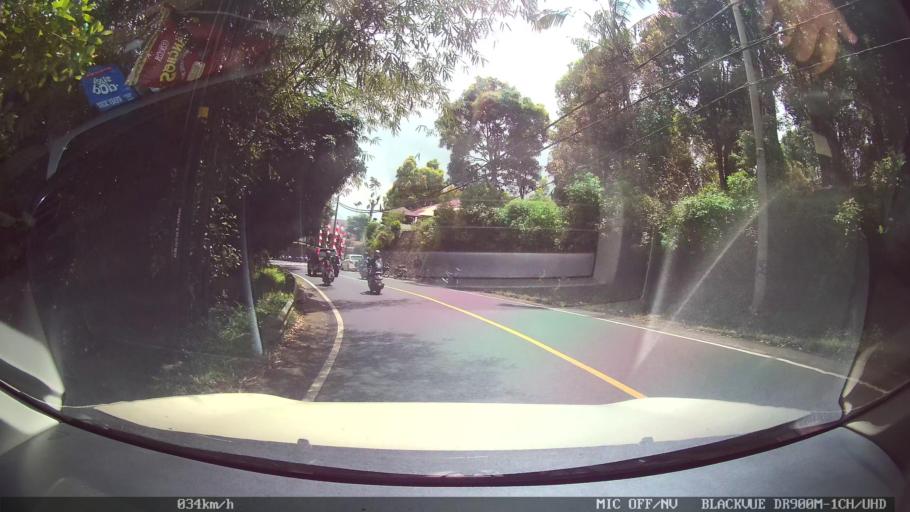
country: ID
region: Bali
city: Banjar Ambengan
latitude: -8.2016
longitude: 115.1406
